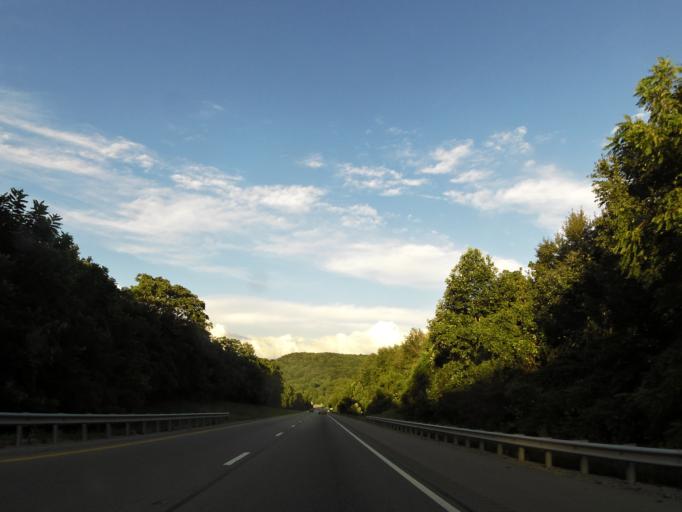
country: US
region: Tennessee
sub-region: Putnam County
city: Algood
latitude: 36.1405
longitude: -85.4325
